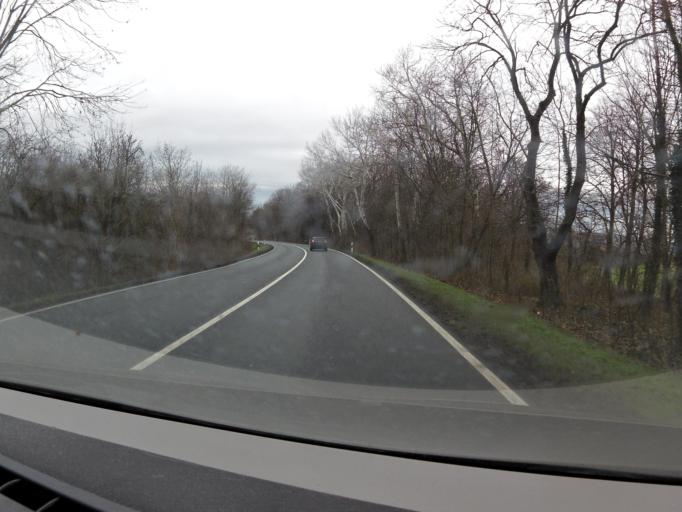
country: DE
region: Saxony-Anhalt
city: Aschersleben
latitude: 51.7403
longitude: 11.4554
